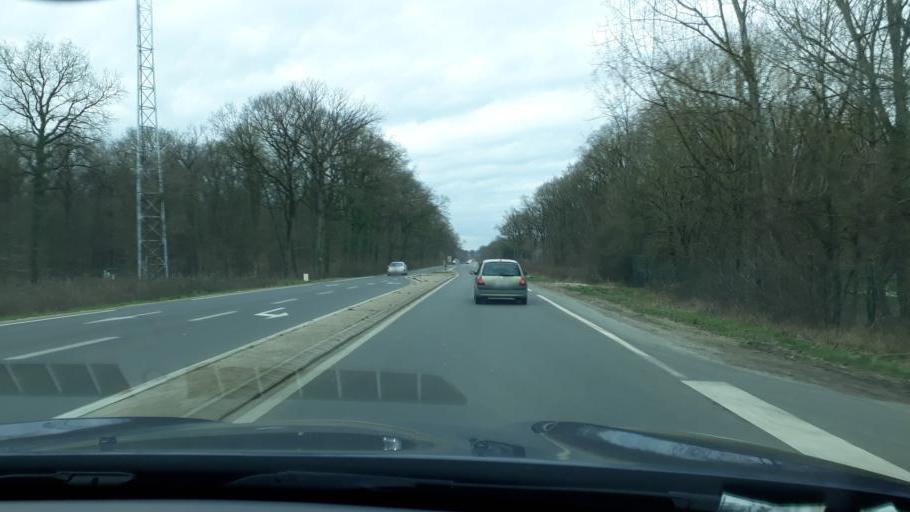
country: FR
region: Centre
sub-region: Departement du Loiret
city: Chanteau
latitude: 48.0095
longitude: 1.9547
